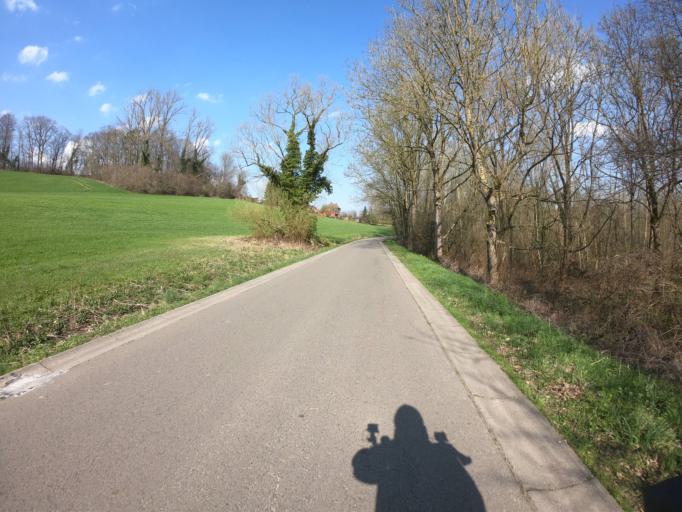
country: BE
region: Flanders
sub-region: Provincie Vlaams-Brabant
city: Overijse
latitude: 50.7491
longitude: 4.5632
